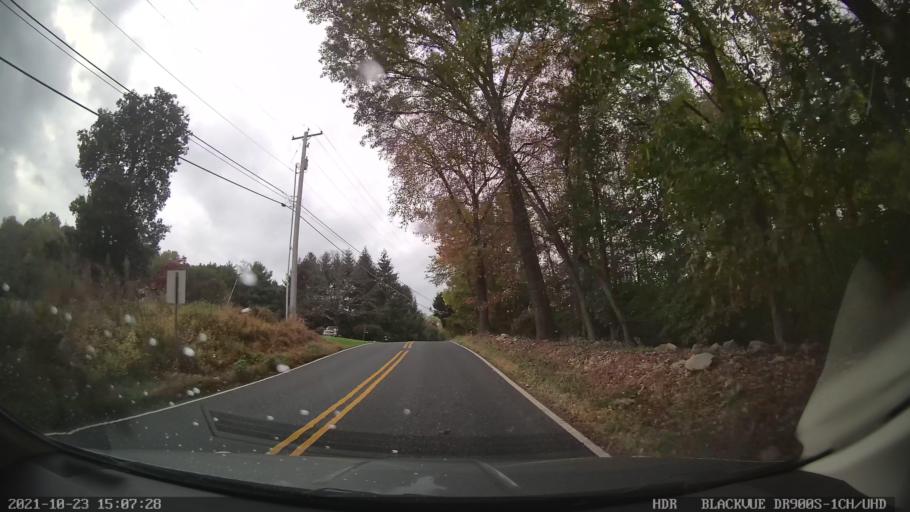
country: US
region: Pennsylvania
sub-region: Berks County
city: Bally
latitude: 40.4381
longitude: -75.6034
